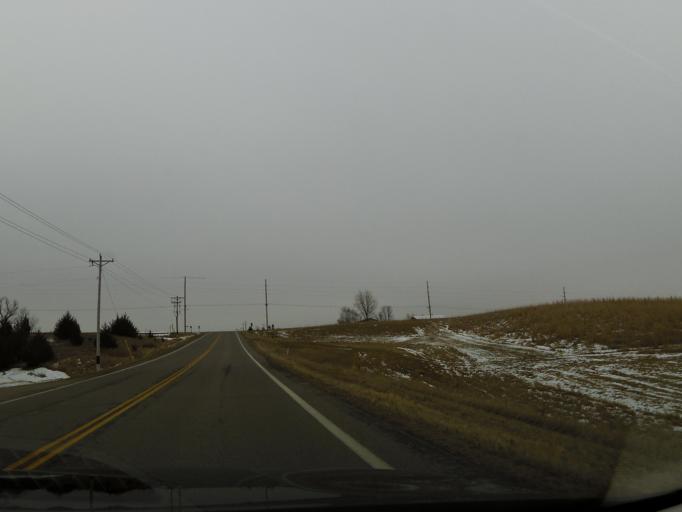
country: US
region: Minnesota
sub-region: Scott County
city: Jordan
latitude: 44.6306
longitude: -93.5651
